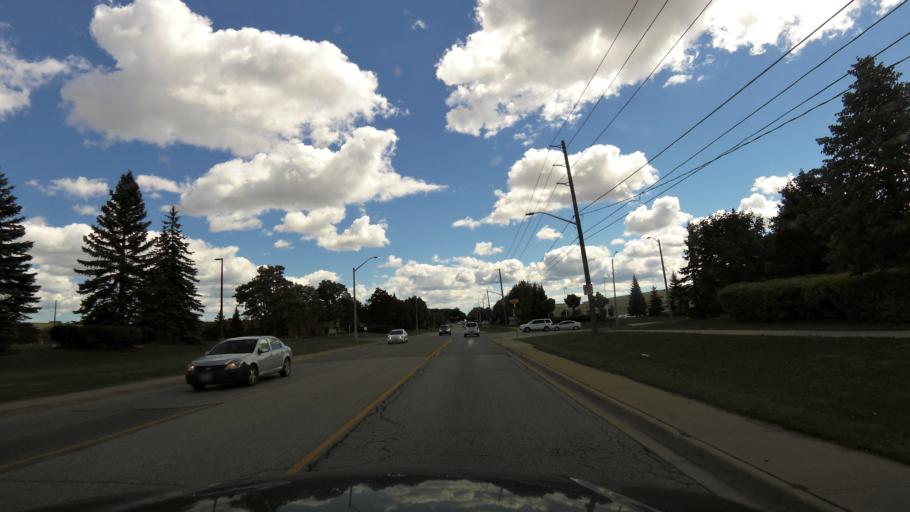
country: CA
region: Ontario
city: Mississauga
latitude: 43.6149
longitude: -79.6879
